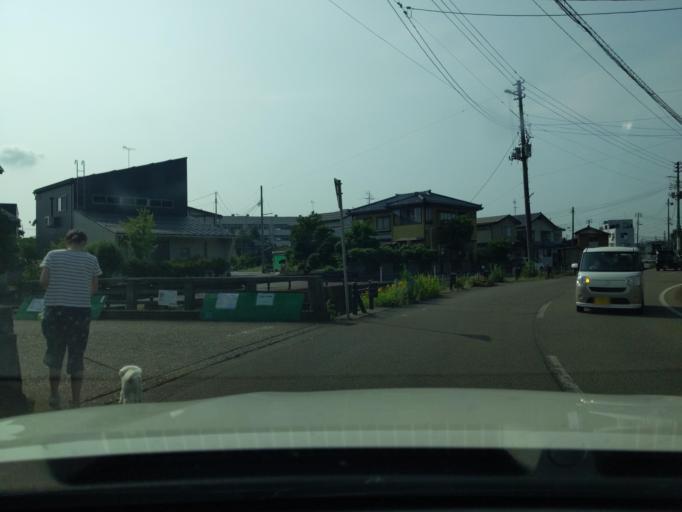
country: JP
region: Niigata
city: Nagaoka
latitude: 37.4354
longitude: 138.8568
